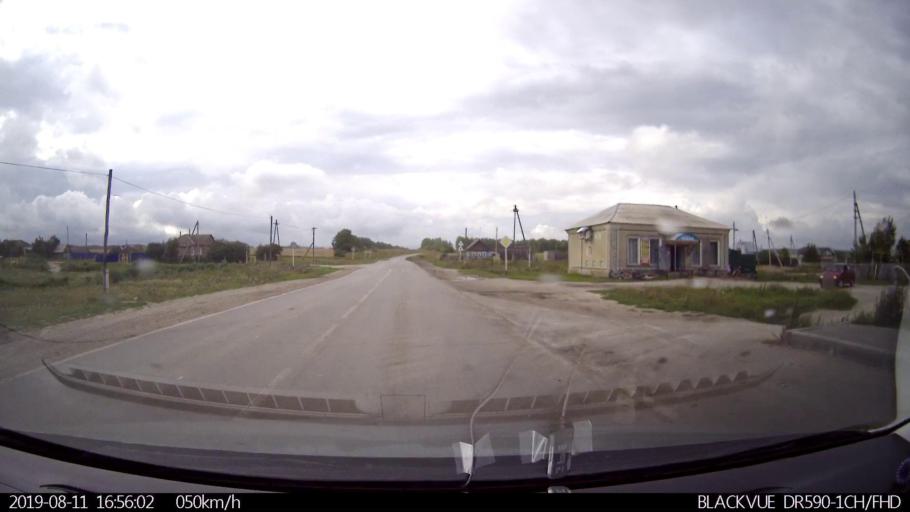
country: RU
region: Ulyanovsk
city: Mayna
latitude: 54.2853
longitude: 47.6577
